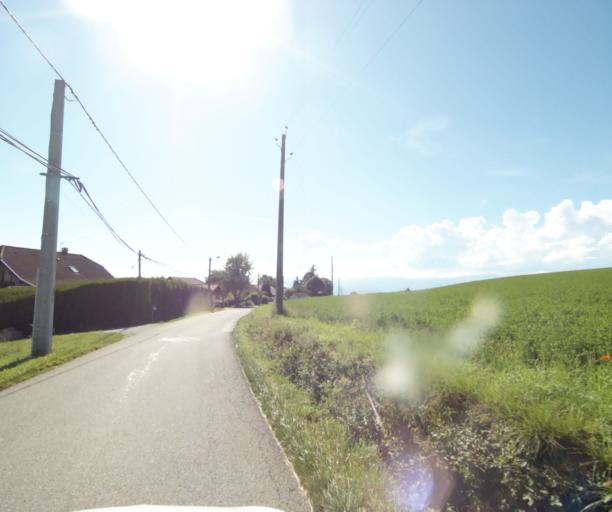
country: FR
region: Rhone-Alpes
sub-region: Departement de la Haute-Savoie
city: Ballaison
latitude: 46.2937
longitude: 6.3368
